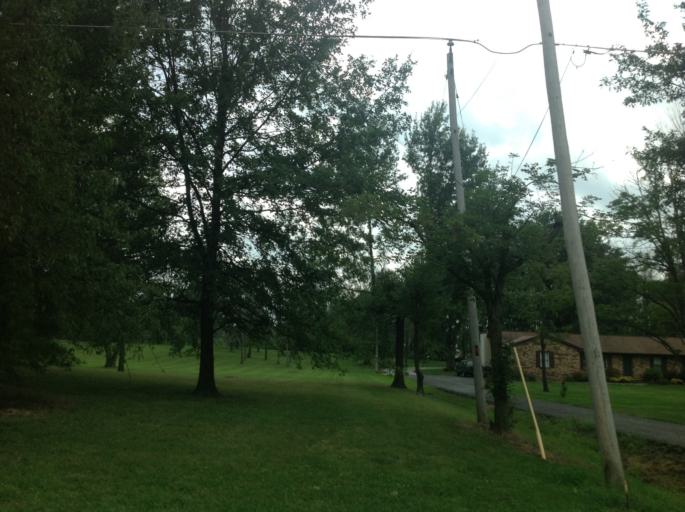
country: US
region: Ohio
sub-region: Franklin County
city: Westerville
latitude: 40.1984
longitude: -82.9204
